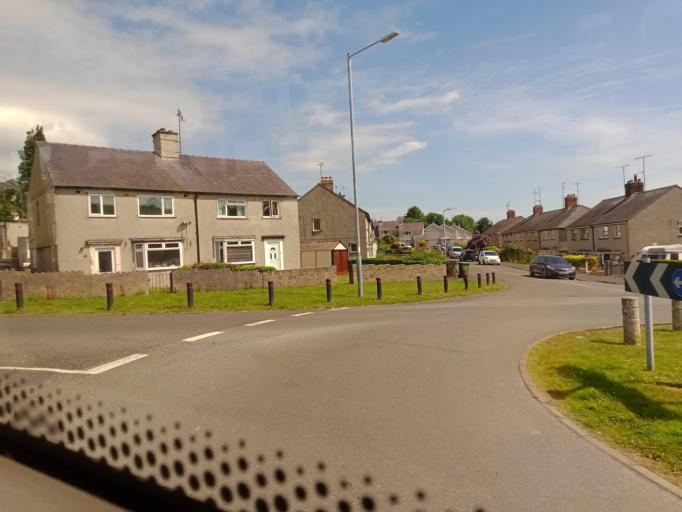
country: GB
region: Wales
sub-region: Gwynedd
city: Bangor
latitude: 53.2148
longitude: -4.1467
